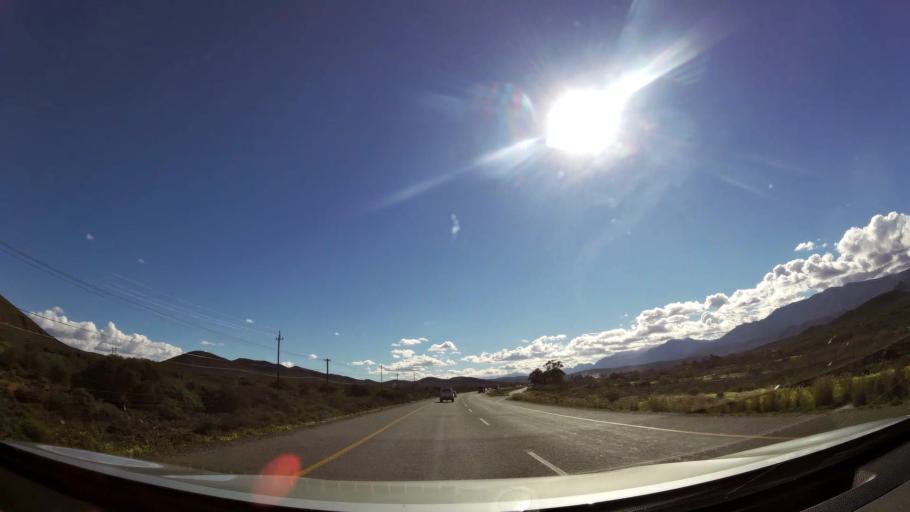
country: ZA
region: Western Cape
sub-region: Cape Winelands District Municipality
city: Ashton
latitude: -33.7750
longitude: 19.7560
